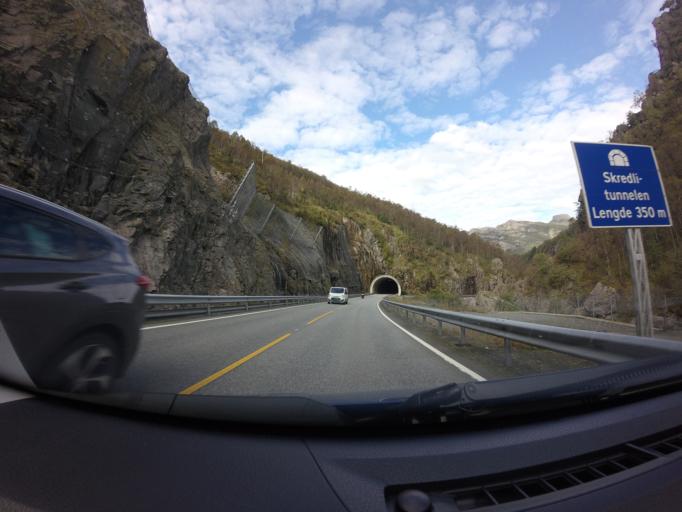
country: NO
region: Rogaland
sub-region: Forsand
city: Forsand
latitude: 58.7920
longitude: 6.2760
